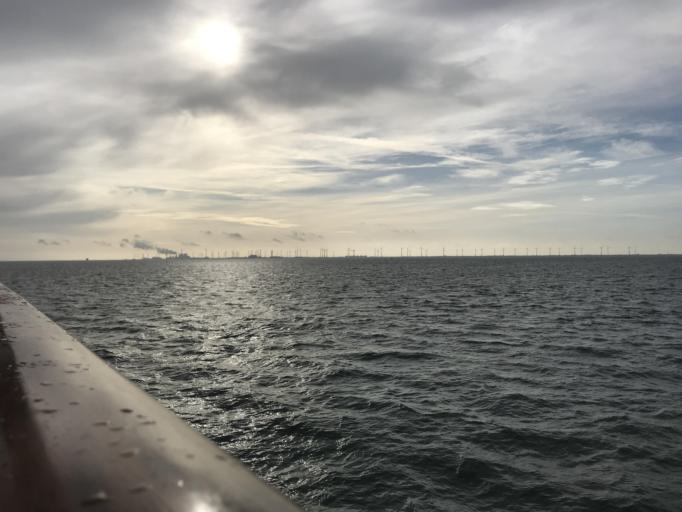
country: DE
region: Lower Saxony
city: Borkum
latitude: 53.5269
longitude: 6.7637
